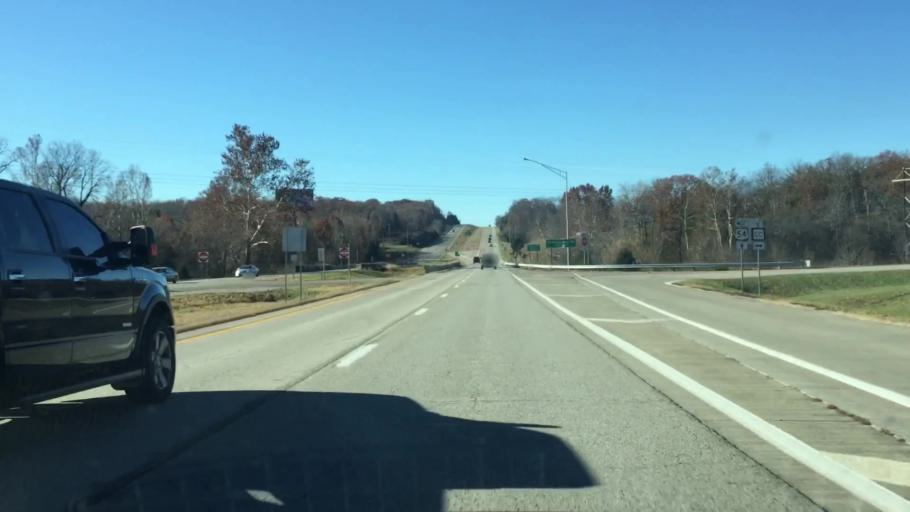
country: US
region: Missouri
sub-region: Cole County
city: Wardsville
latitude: 38.5206
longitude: -92.2317
